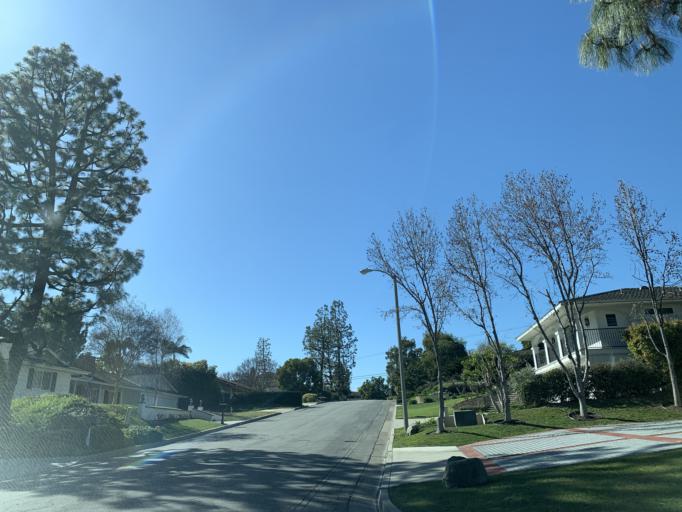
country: US
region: California
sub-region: Orange County
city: Placentia
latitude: 33.8865
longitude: -117.8968
